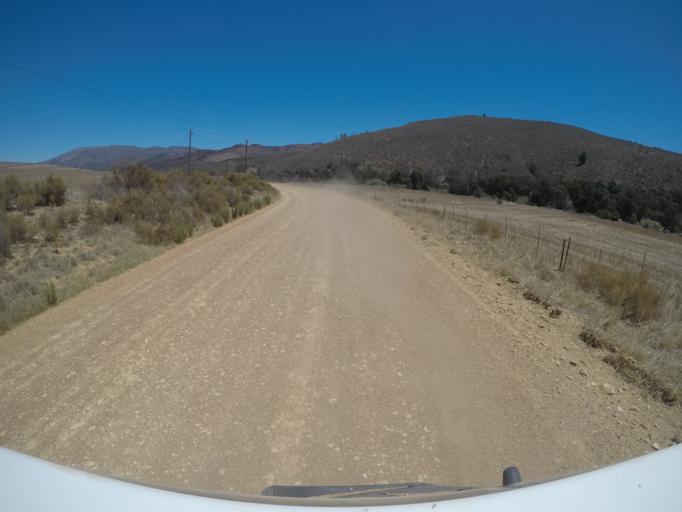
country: ZA
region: Western Cape
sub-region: Overberg District Municipality
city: Caledon
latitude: -34.1482
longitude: 19.2431
